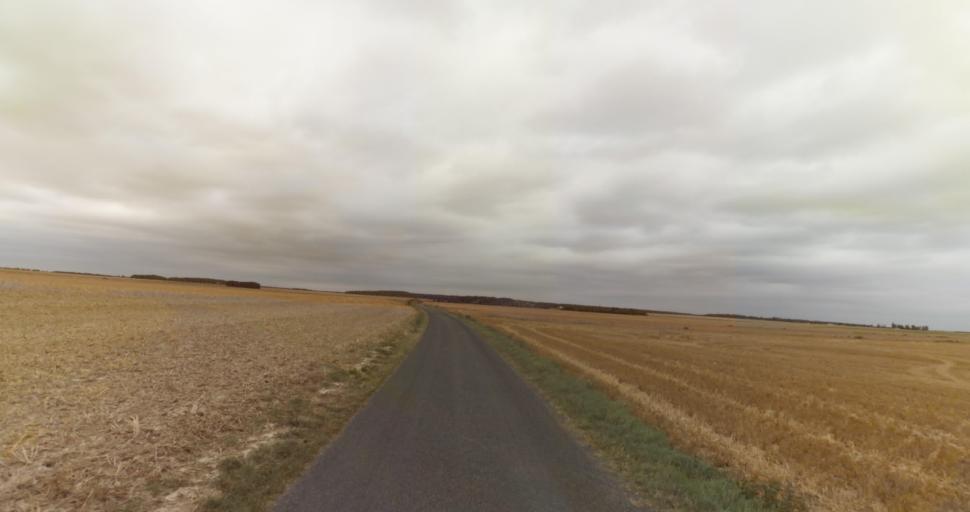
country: FR
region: Haute-Normandie
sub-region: Departement de l'Eure
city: La Couture-Boussey
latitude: 48.9399
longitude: 1.3358
